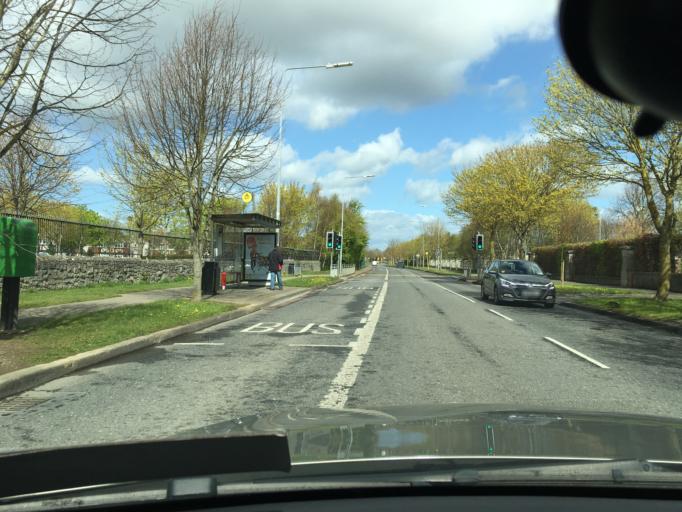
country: IE
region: Leinster
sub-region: Fingal County
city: Blanchardstown
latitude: 53.3725
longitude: -6.3884
